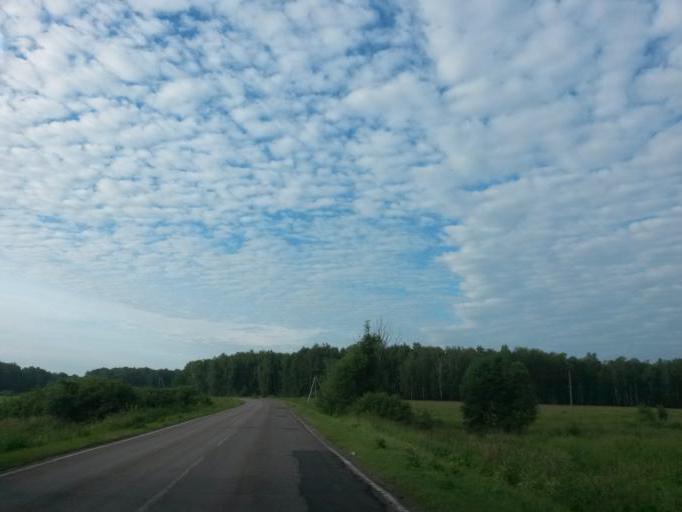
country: RU
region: Moskovskaya
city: Lyubuchany
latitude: 55.2358
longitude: 37.6436
